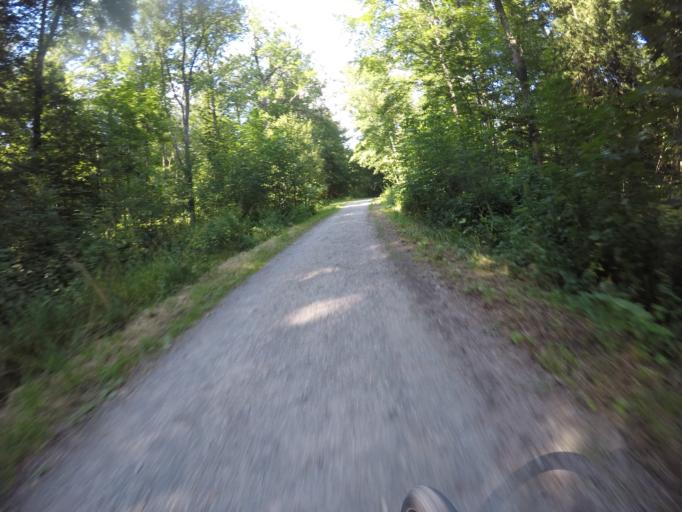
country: DE
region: Baden-Wuerttemberg
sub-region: Regierungsbezirk Stuttgart
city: Boeblingen
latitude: 48.6621
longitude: 8.9887
